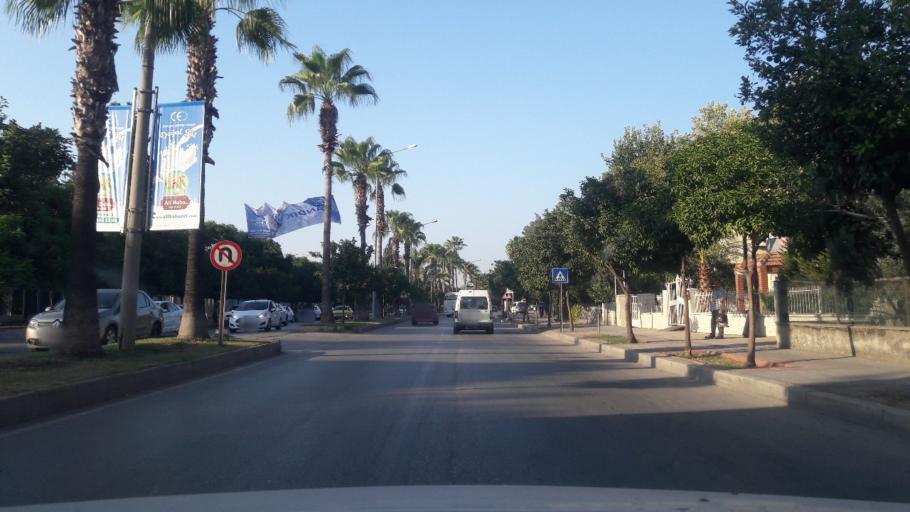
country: TR
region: Adana
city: Seyhan
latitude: 36.9885
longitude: 35.2981
